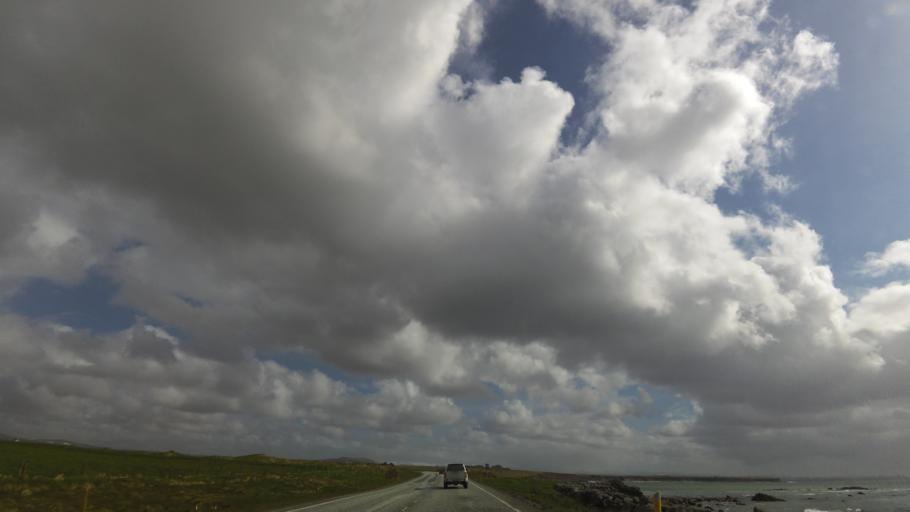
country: IS
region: Capital Region
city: Reykjavik
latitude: 64.2285
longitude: -21.8152
